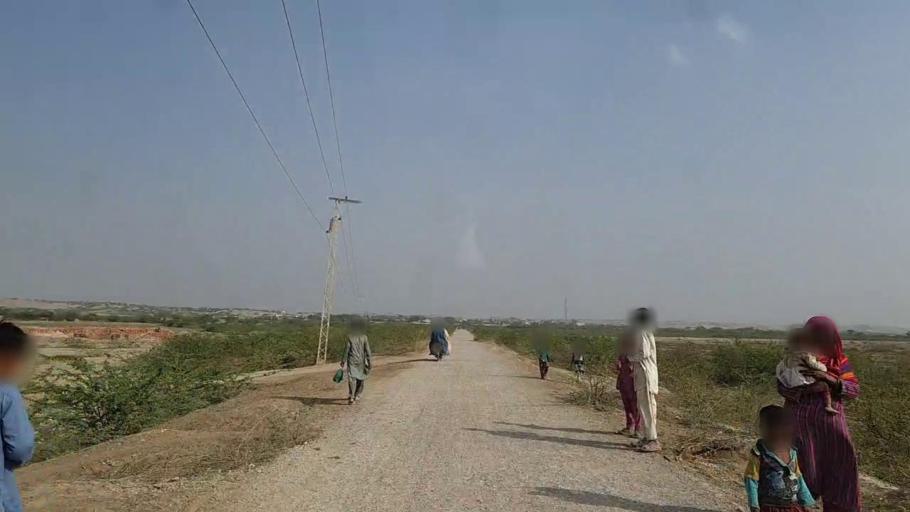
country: PK
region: Sindh
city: Naukot
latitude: 24.6637
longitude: 69.2816
